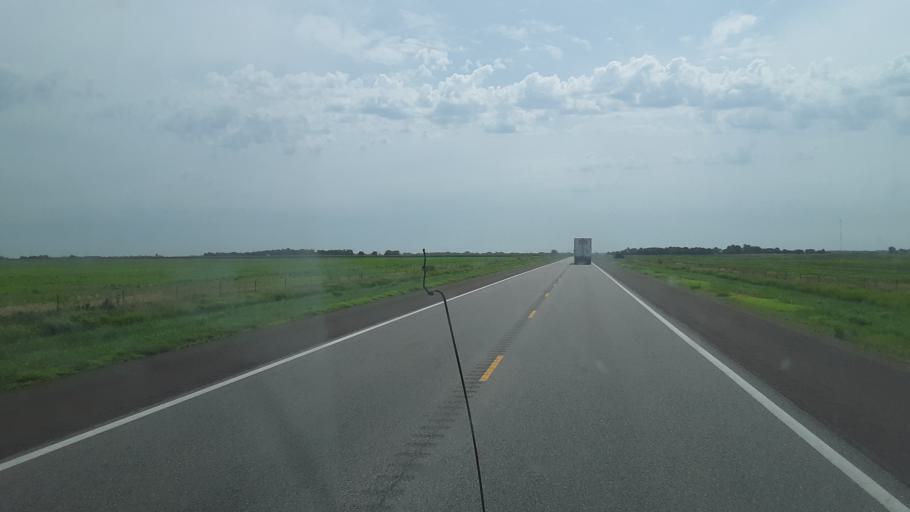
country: US
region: Kansas
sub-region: Reno County
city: Nickerson
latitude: 37.9851
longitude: -98.1035
